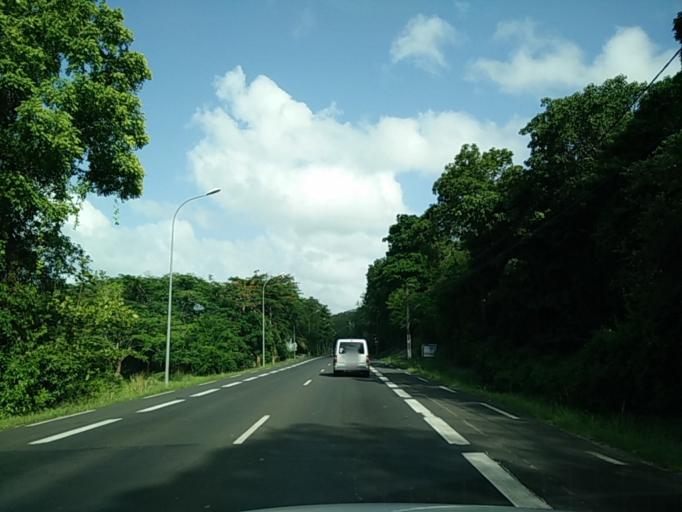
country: GP
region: Guadeloupe
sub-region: Guadeloupe
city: Le Gosier
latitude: 16.2173
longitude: -61.4837
